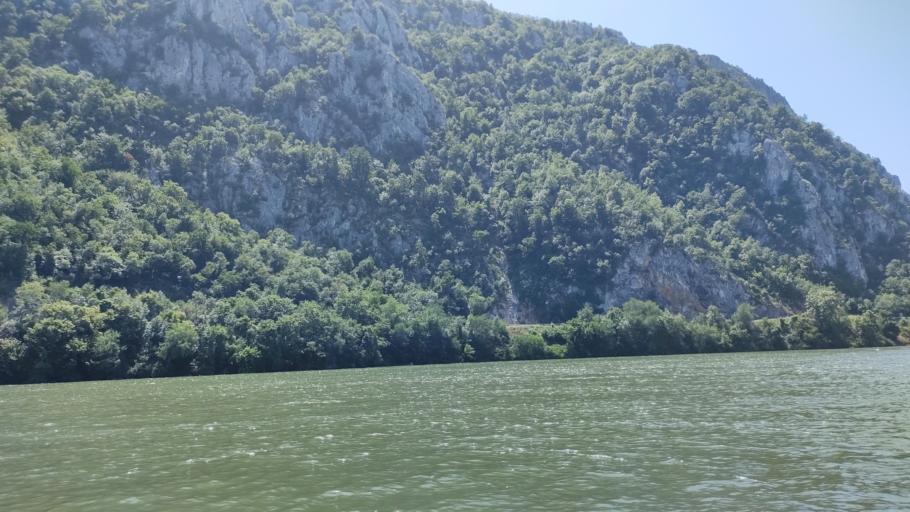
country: RO
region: Mehedinti
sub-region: Comuna Dubova
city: Dubova
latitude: 44.6236
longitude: 22.2763
